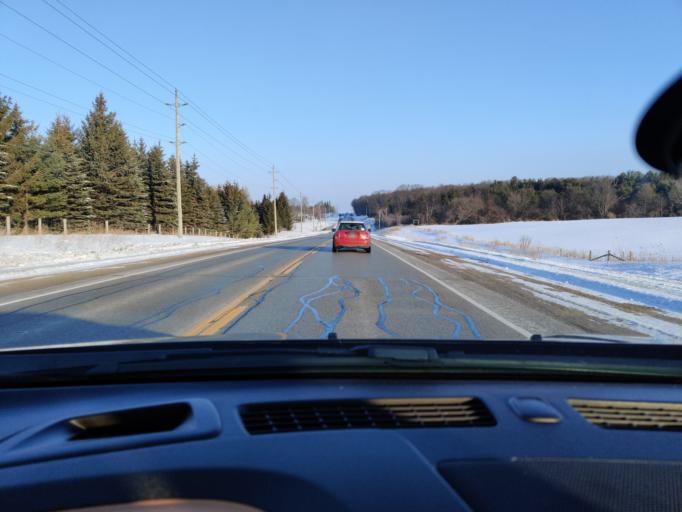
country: CA
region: Ontario
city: Angus
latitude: 44.3893
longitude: -79.7945
